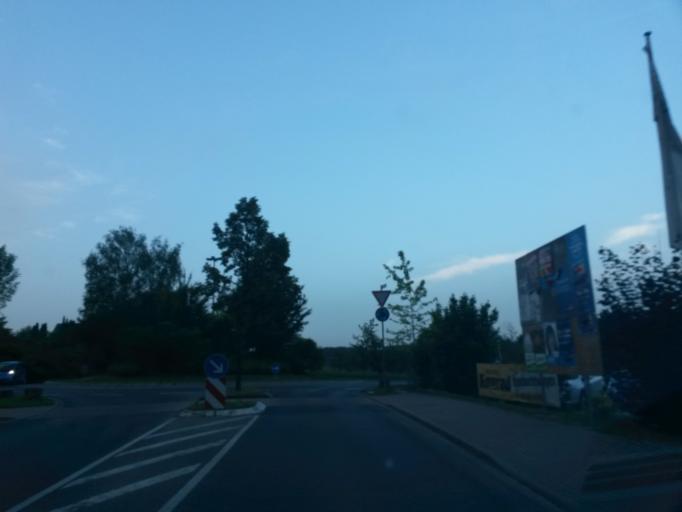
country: DE
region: Bavaria
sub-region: Regierungsbezirk Unterfranken
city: Estenfeld
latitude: 49.8340
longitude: 10.0097
